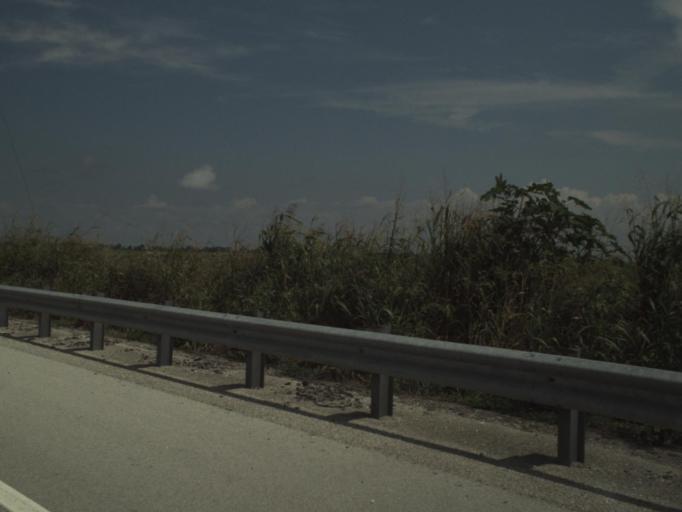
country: US
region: Florida
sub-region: Palm Beach County
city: Pahokee
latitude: 26.8483
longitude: -80.6102
